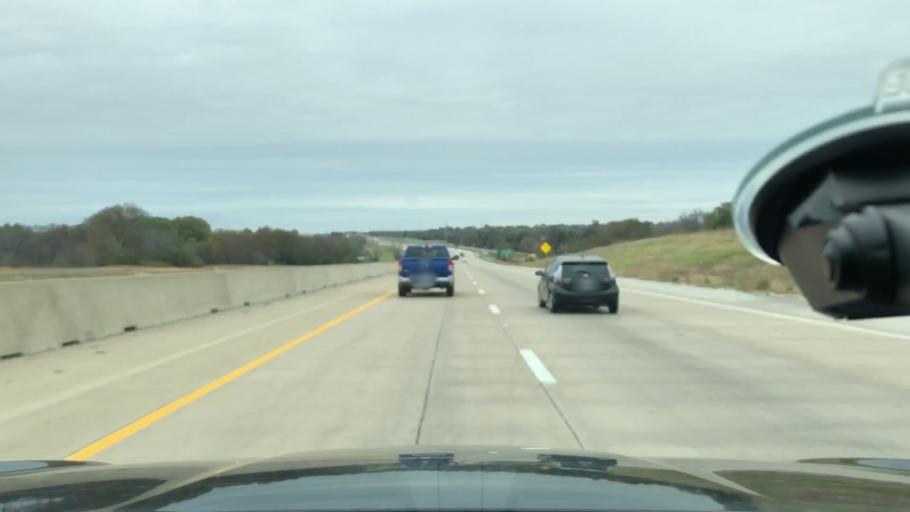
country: US
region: Texas
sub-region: Ellis County
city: Waxahachie
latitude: 32.3421
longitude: -96.8556
